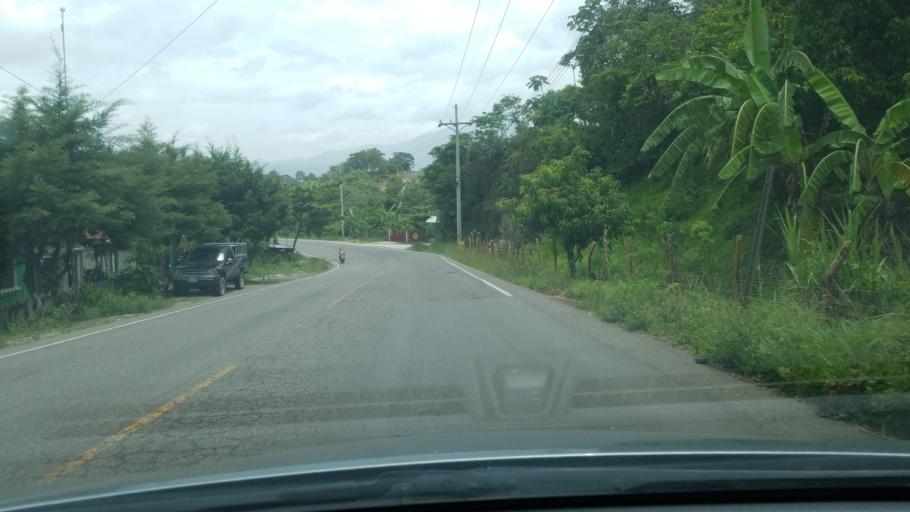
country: HN
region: Copan
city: Ojos de Agua
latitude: 14.6723
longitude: -88.8388
